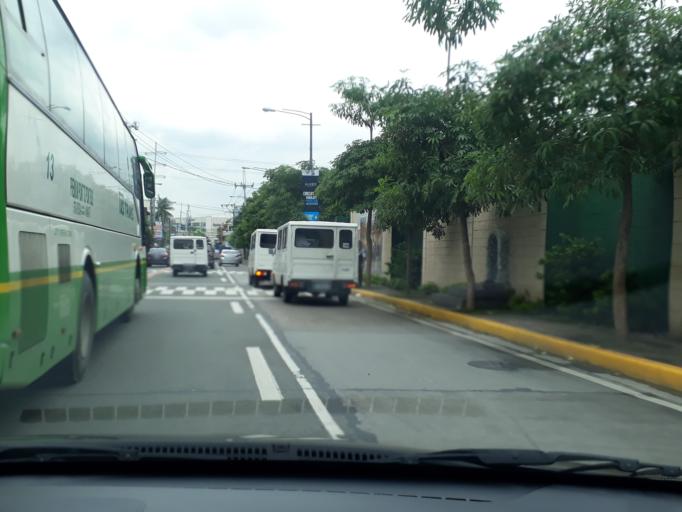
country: PH
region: Metro Manila
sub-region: Makati City
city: Makati City
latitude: 14.5671
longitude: 121.0176
